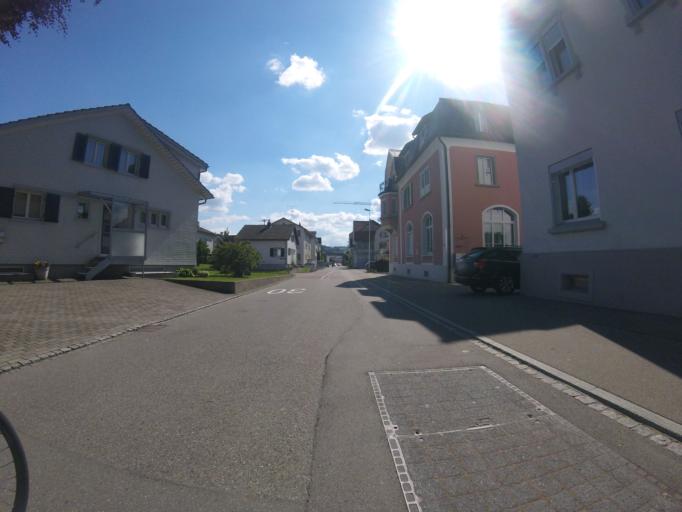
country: CH
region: Saint Gallen
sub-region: Wahlkreis St. Gallen
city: Gossau
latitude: 47.4127
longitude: 9.2463
